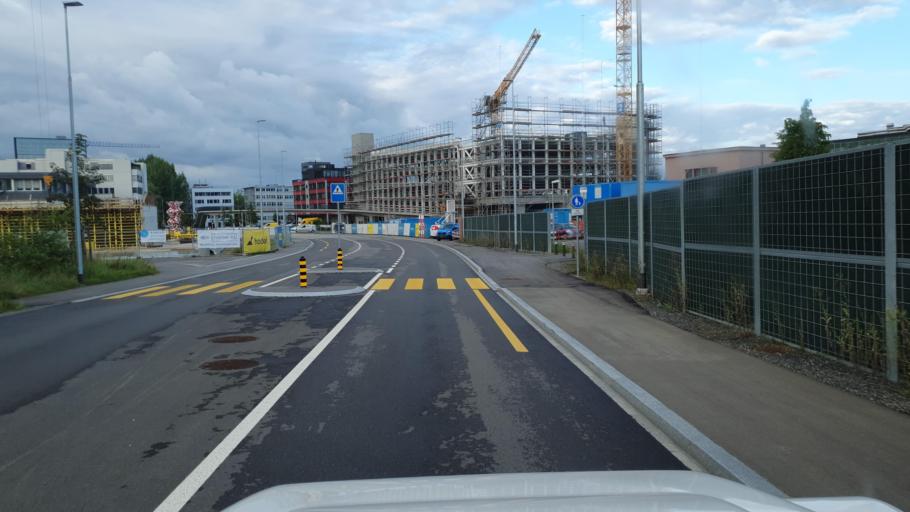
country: CH
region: Zug
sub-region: Zug
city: Baar
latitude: 47.1855
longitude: 8.5233
